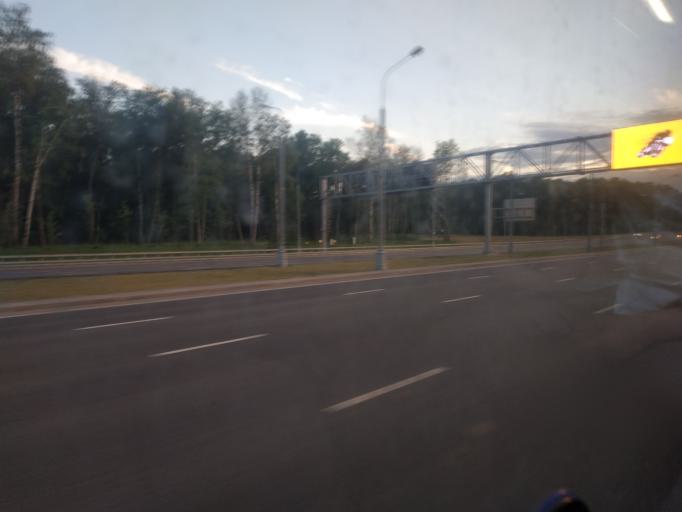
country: RU
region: Moscow
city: Solntsevo
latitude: 55.6104
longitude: 37.3881
